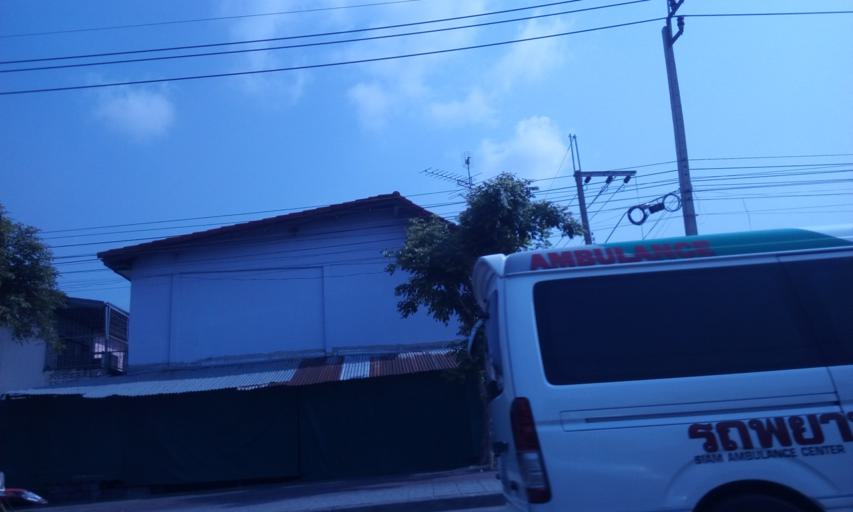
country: TH
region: Bangkok
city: Bang Khen
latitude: 13.8856
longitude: 100.6182
